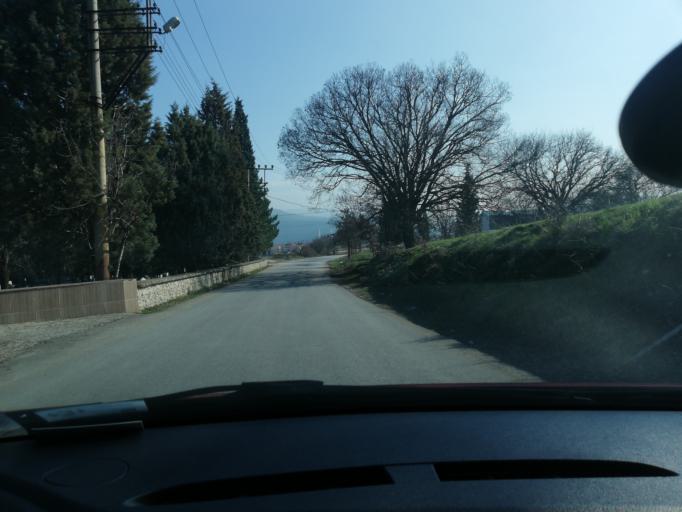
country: TR
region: Karabuk
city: Safranbolu
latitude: 41.2468
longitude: 32.6588
